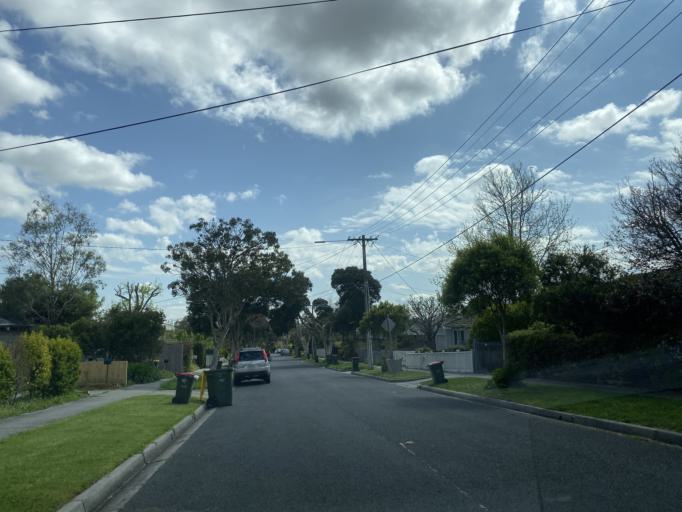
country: AU
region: Victoria
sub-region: Whitehorse
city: Burwood
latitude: -37.8479
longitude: 145.1247
